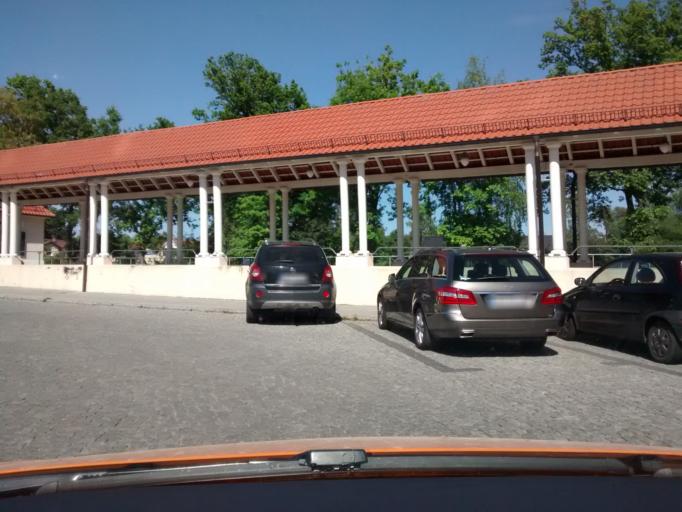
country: DE
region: Brandenburg
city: Bad Saarow
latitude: 52.2928
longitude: 14.0645
